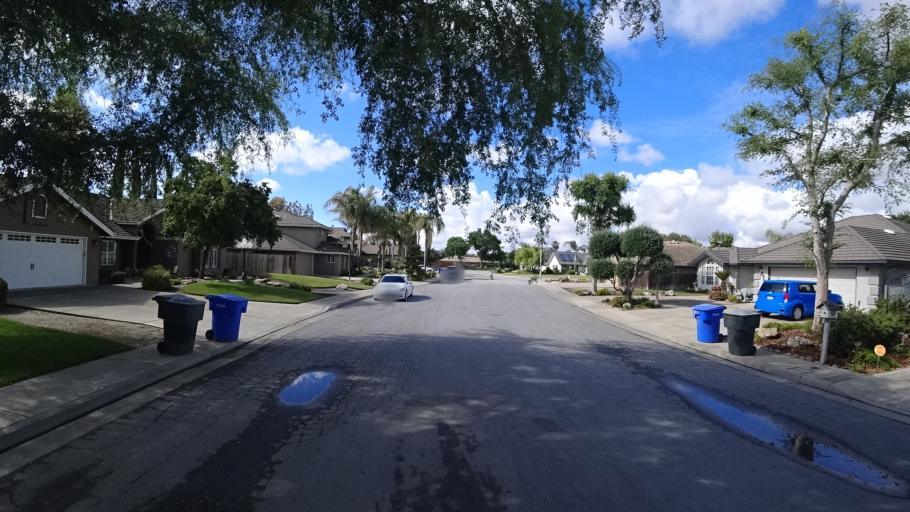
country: US
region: California
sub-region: Kings County
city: Lucerne
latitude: 36.3601
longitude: -119.6448
